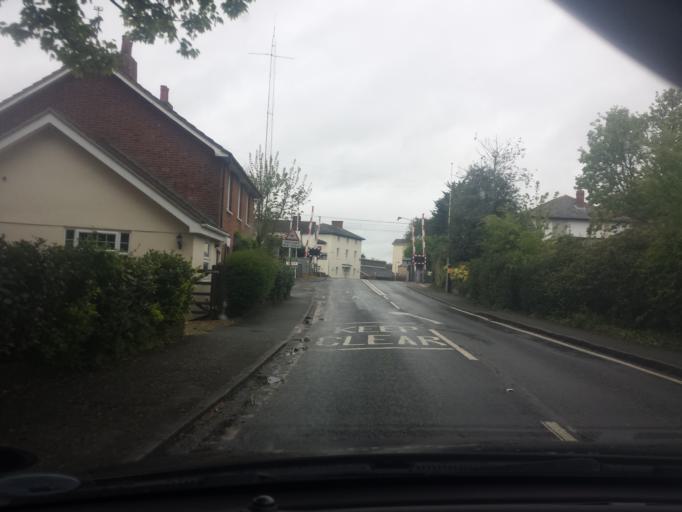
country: GB
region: England
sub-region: Suffolk
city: East Bergholt
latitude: 51.9213
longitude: 0.9862
